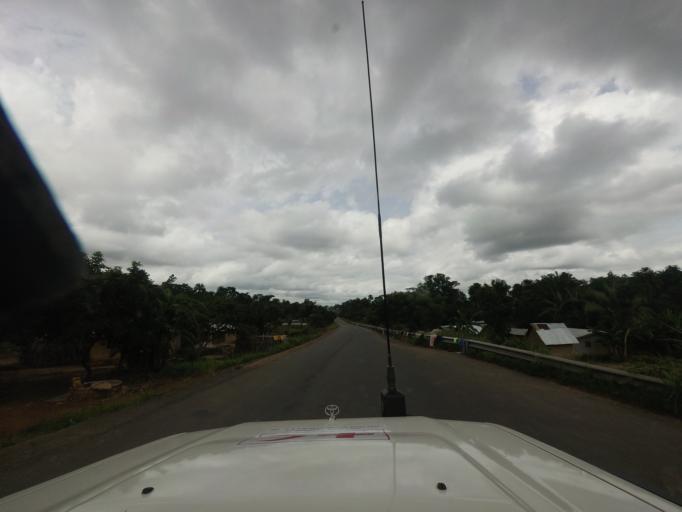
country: GN
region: Nzerekore
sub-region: Macenta
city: Macenta
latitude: 8.2824
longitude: -9.1776
